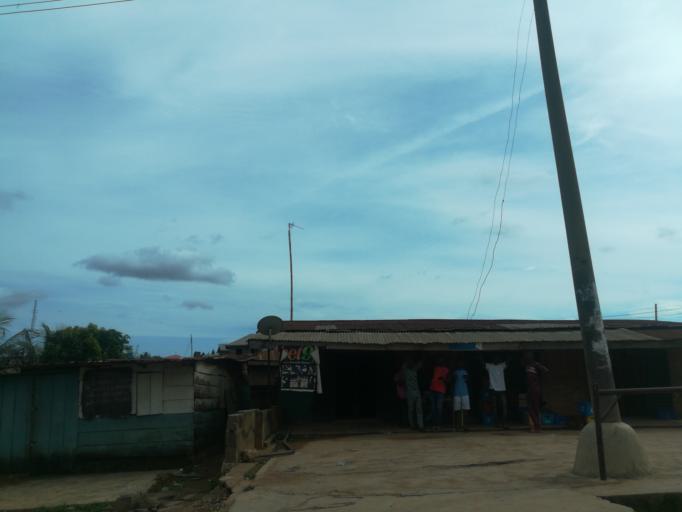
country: NG
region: Oyo
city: Ibadan
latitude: 7.3776
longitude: 3.9543
